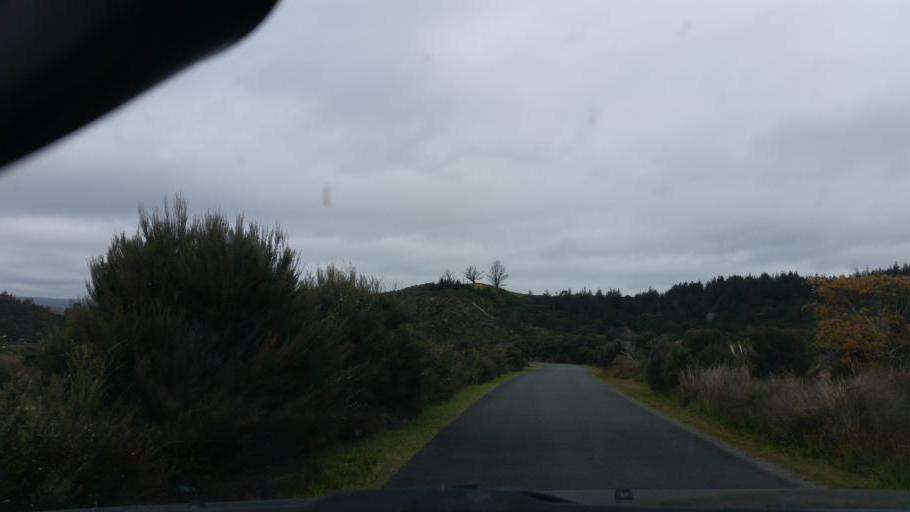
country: NZ
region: Northland
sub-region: Kaipara District
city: Dargaville
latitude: -35.8122
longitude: 173.6574
